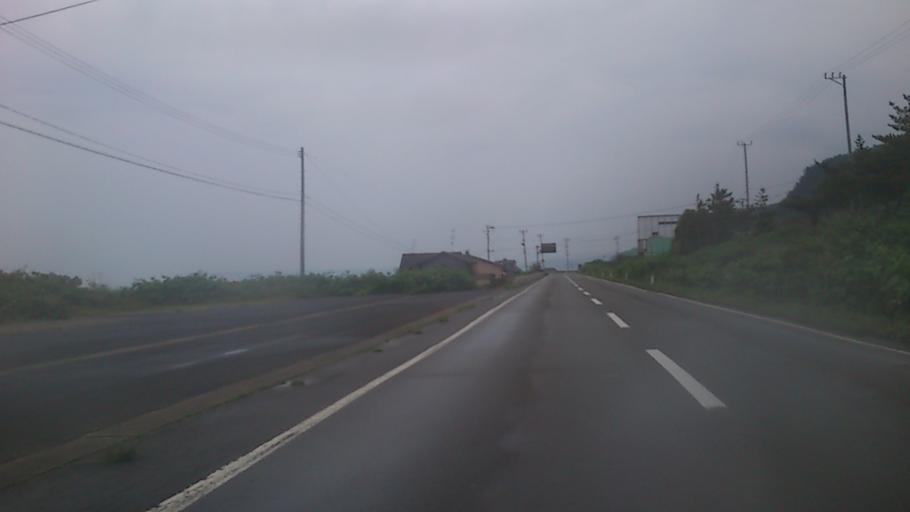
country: JP
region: Akita
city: Noshiromachi
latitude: 40.4549
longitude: 139.9428
